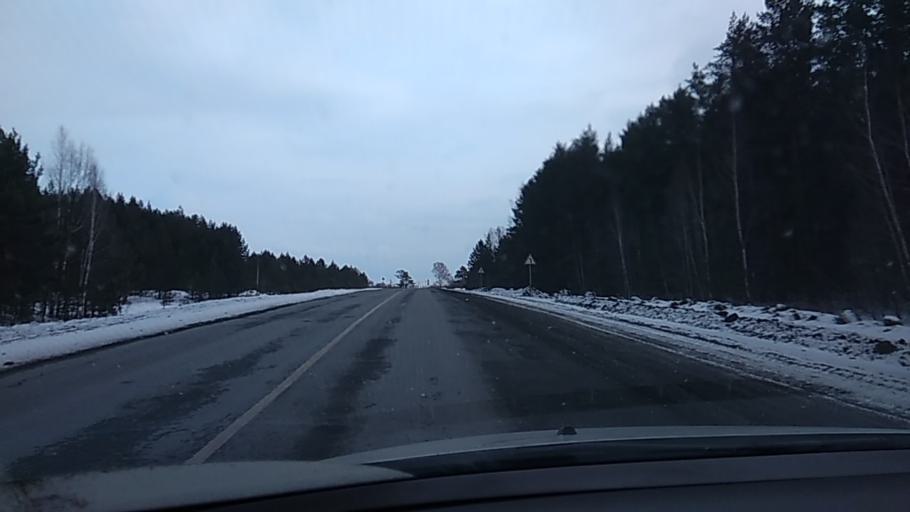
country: RU
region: Sverdlovsk
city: Dvurechensk
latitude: 56.6320
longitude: 61.2654
